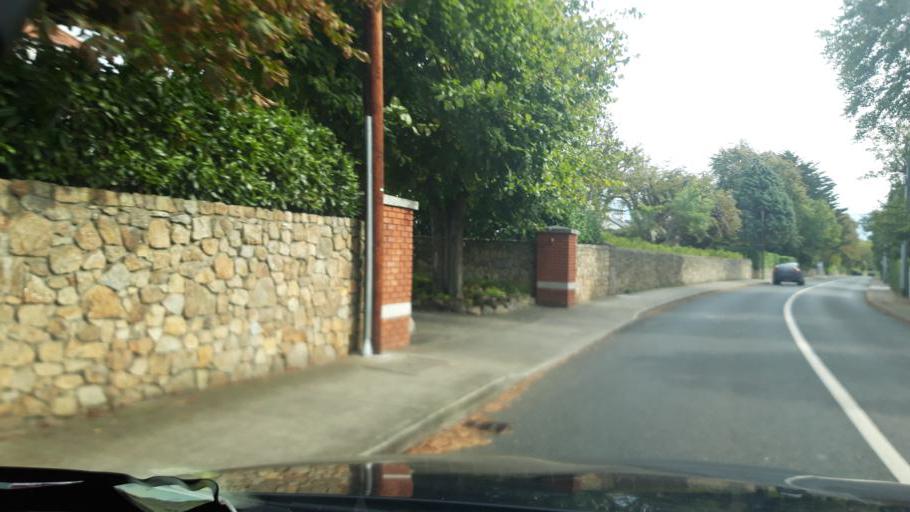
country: IE
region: Leinster
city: Foxrock
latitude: 53.2732
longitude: -6.1897
